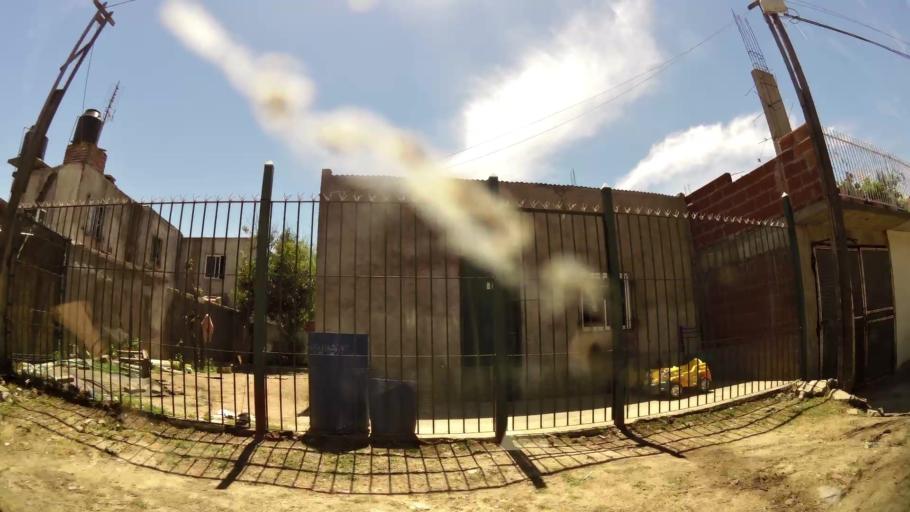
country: AR
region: Buenos Aires
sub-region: Partido de Quilmes
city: Quilmes
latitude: -34.7413
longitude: -58.3087
